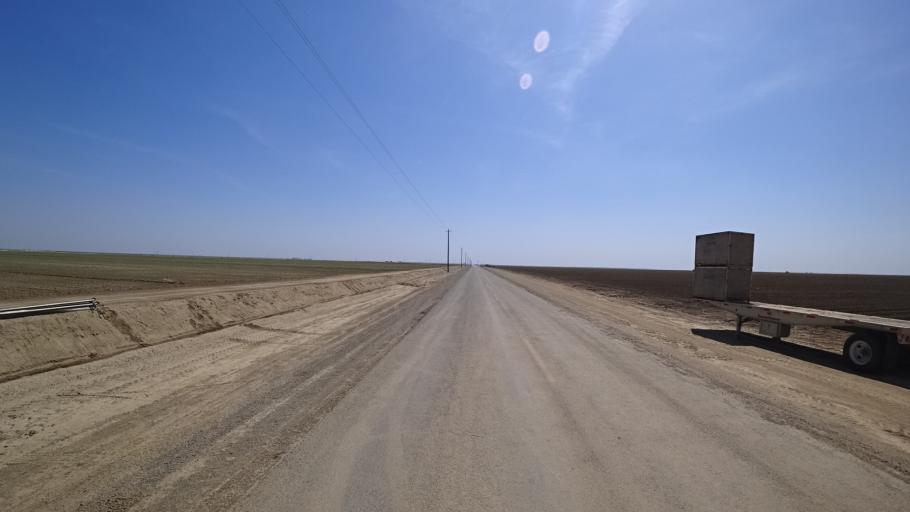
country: US
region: California
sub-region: Kings County
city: Kettleman City
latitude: 36.0942
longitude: -119.9586
